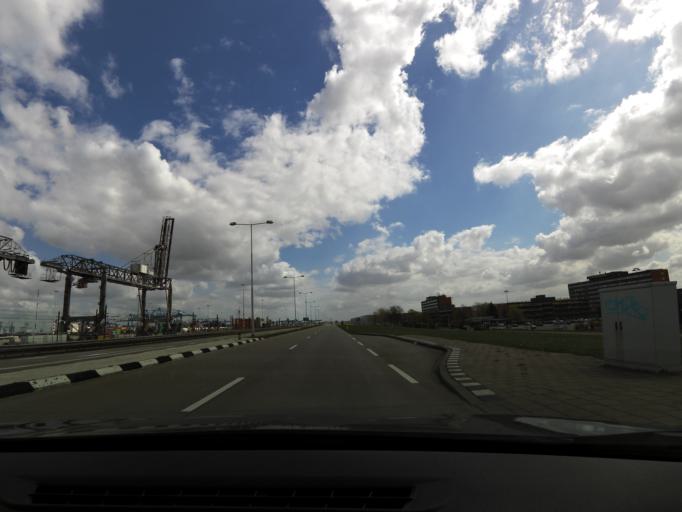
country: NL
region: South Holland
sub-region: Gemeente Albrandswaard
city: Rhoon
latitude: 51.8769
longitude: 4.4000
